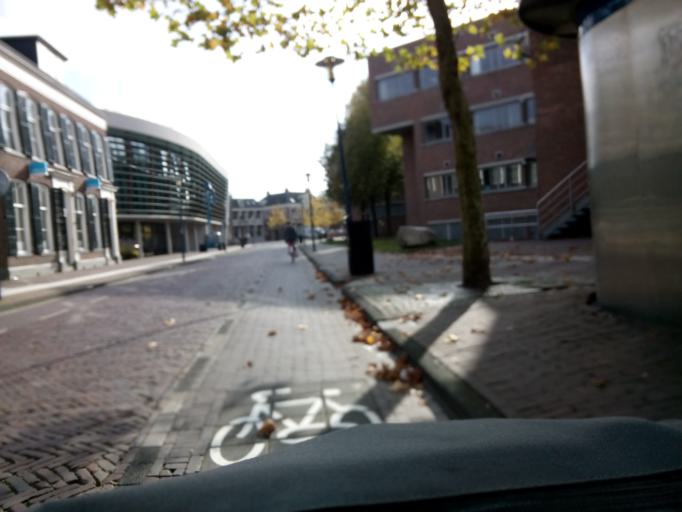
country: NL
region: Drenthe
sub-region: Gemeente Assen
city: Assen
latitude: 52.9949
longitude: 6.5642
